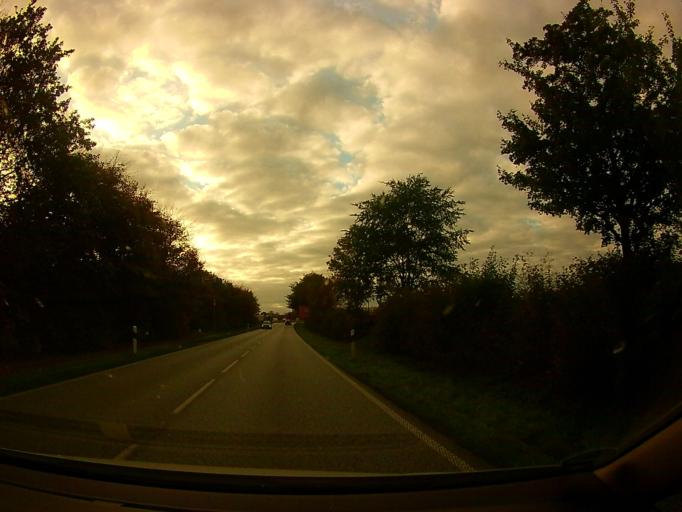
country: DE
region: Schleswig-Holstein
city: Schuby
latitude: 54.5189
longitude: 9.4690
